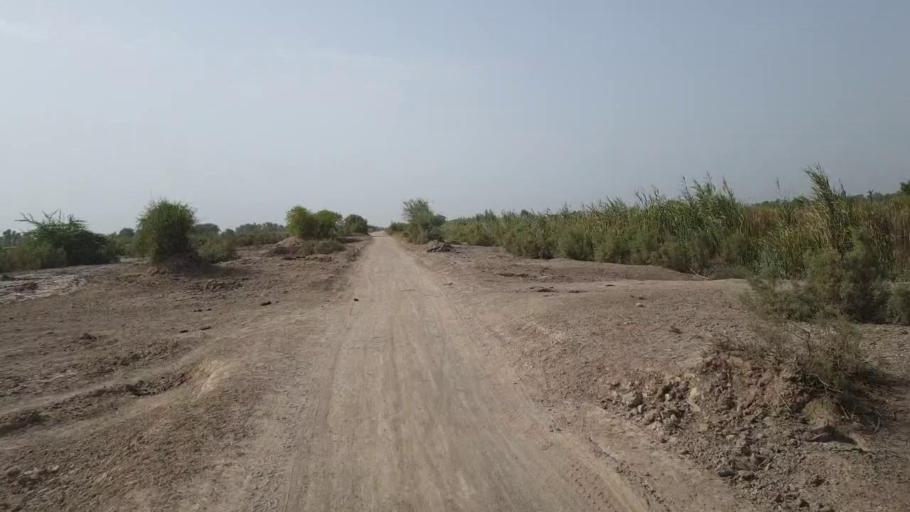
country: PK
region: Sindh
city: Daur
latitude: 26.4118
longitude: 68.1611
